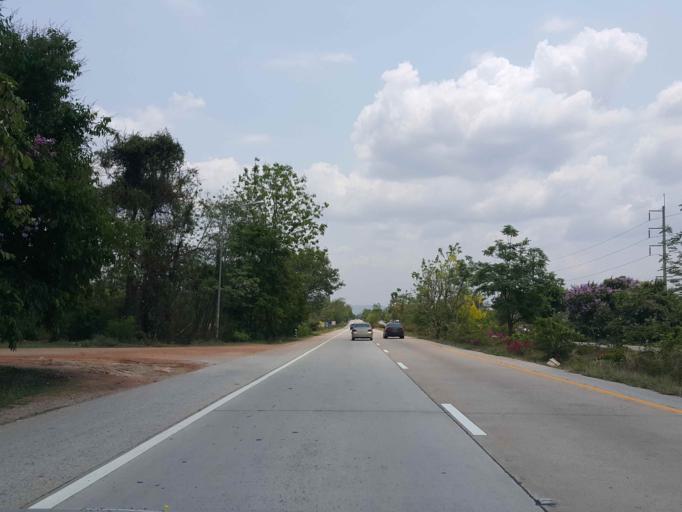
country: TH
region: Lampang
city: Hang Chat
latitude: 18.3008
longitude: 99.4072
